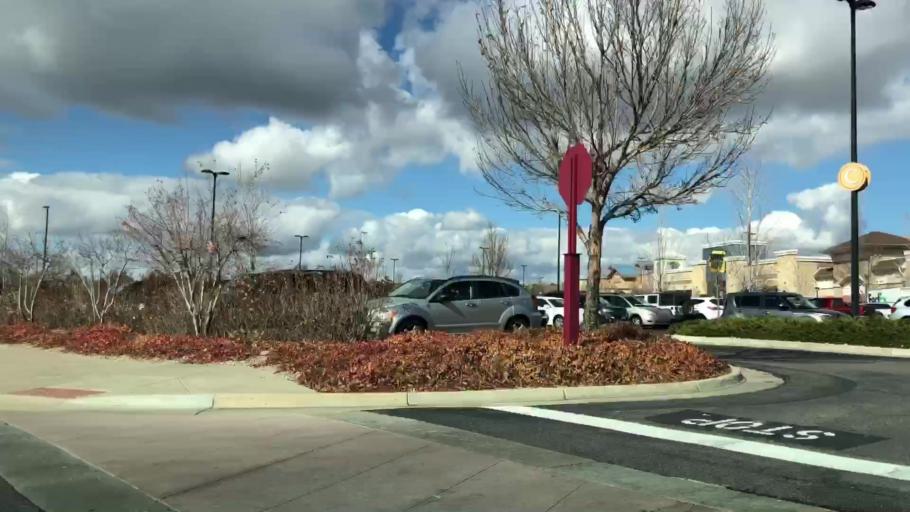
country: US
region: Colorado
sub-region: Larimer County
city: Loveland
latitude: 40.4181
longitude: -104.9887
